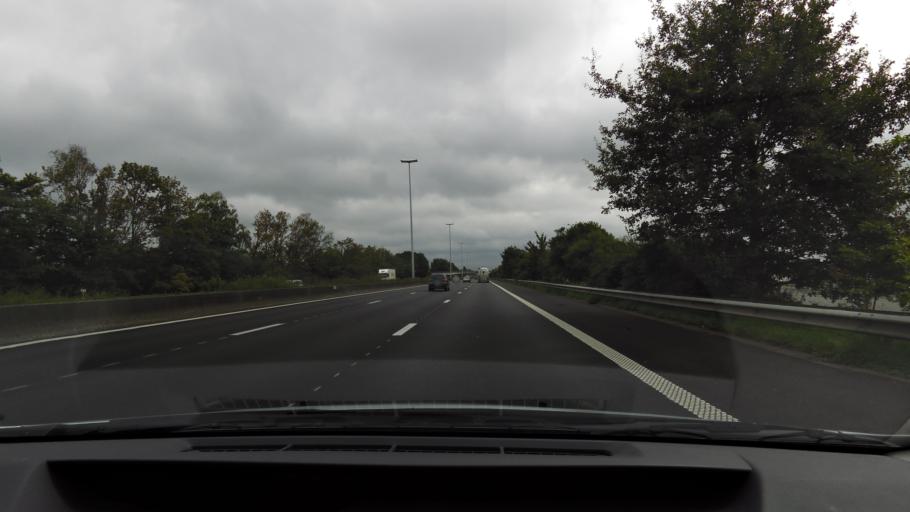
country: BE
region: Flanders
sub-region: Provincie Oost-Vlaanderen
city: Nevele
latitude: 51.0477
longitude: 3.5819
